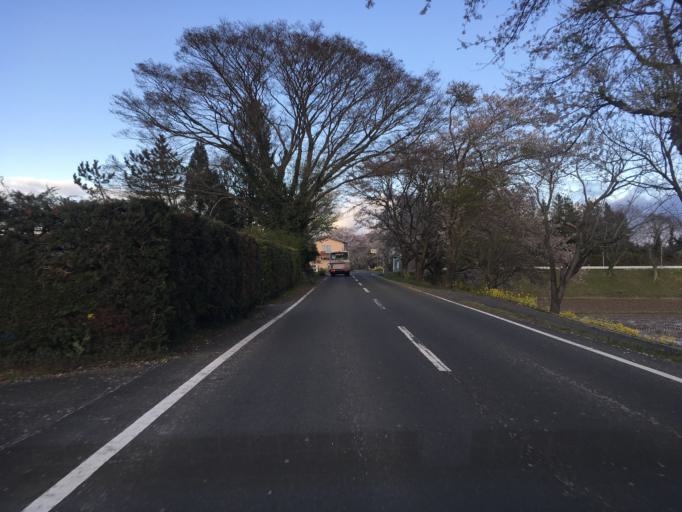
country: JP
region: Miyagi
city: Wakuya
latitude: 38.6460
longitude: 141.1715
